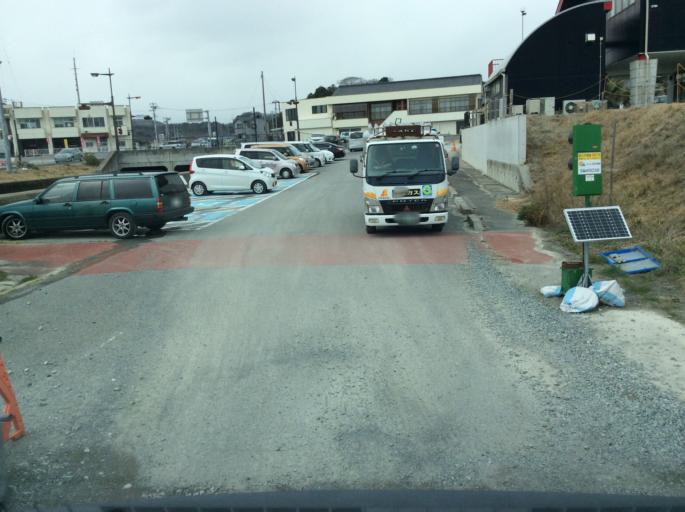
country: JP
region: Fukushima
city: Iwaki
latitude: 37.1070
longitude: 140.9929
